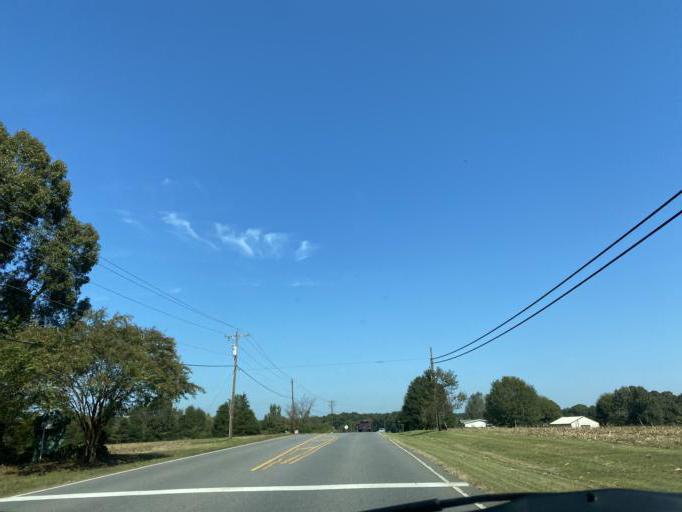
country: US
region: North Carolina
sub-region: Cleveland County
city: Boiling Springs
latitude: 35.2735
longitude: -81.6661
